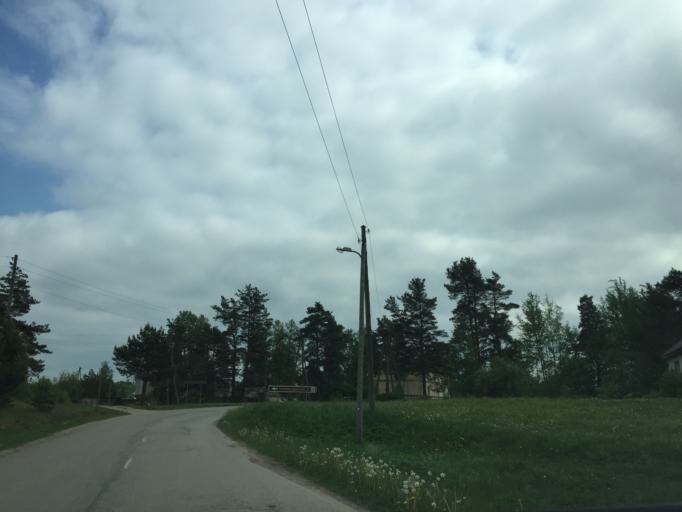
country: LV
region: Rezekne
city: Rezekne
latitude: 56.3454
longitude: 27.1670
